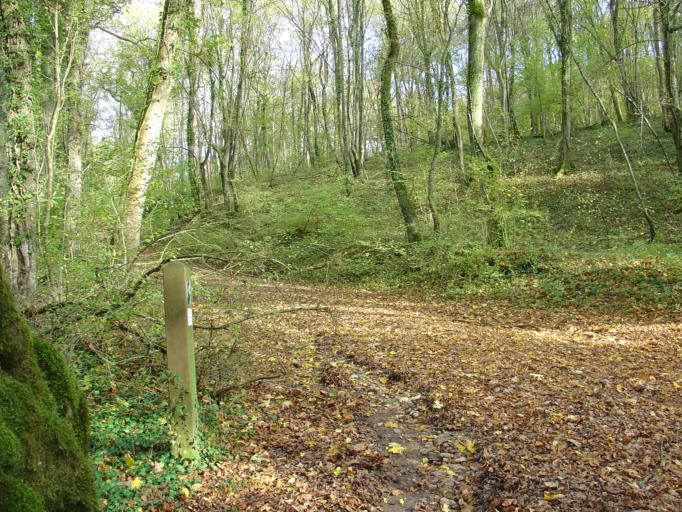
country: FR
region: Lorraine
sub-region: Departement de Meurthe-et-Moselle
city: Saizerais
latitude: 48.8305
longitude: 5.9718
